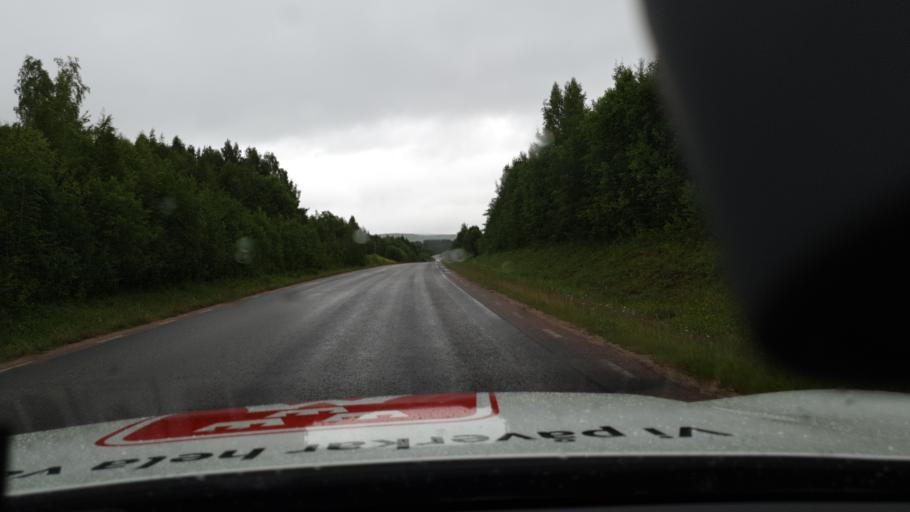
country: SE
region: Norrbotten
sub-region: Overtornea Kommun
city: OEvertornea
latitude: 66.4502
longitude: 23.6192
